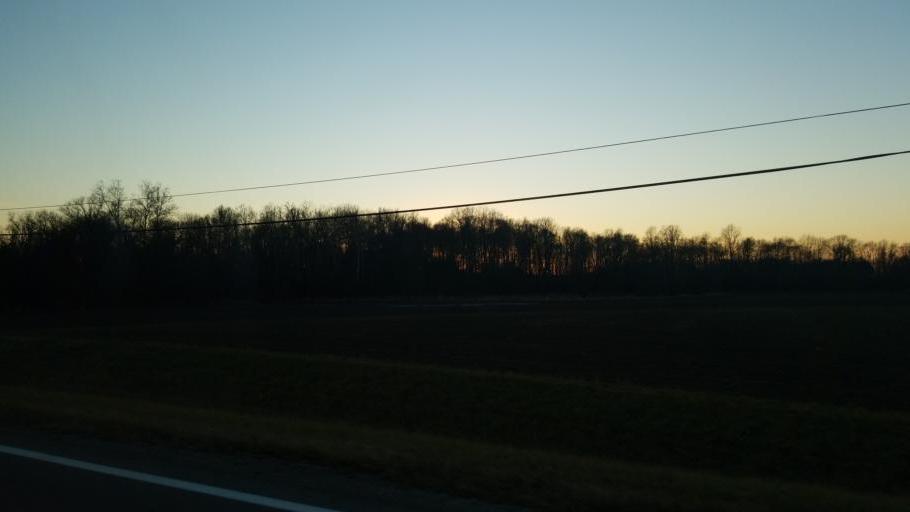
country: US
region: Ohio
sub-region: Wyandot County
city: Upper Sandusky
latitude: 40.8295
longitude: -83.1315
